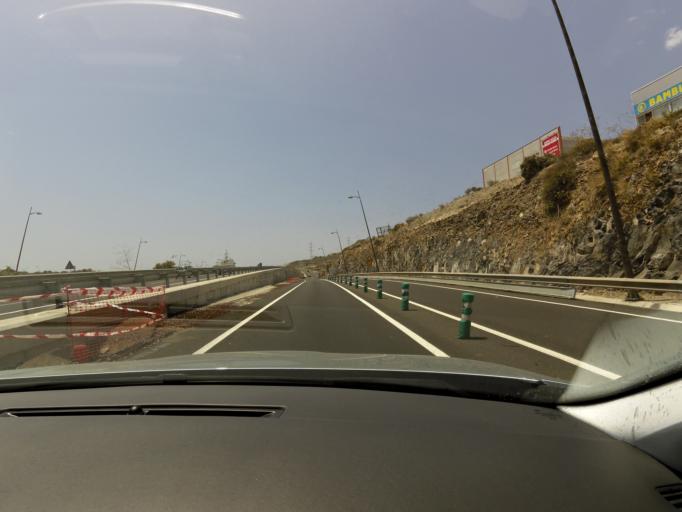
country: ES
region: Canary Islands
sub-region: Provincia de Santa Cruz de Tenerife
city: Adeje
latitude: 28.1258
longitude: -16.7426
